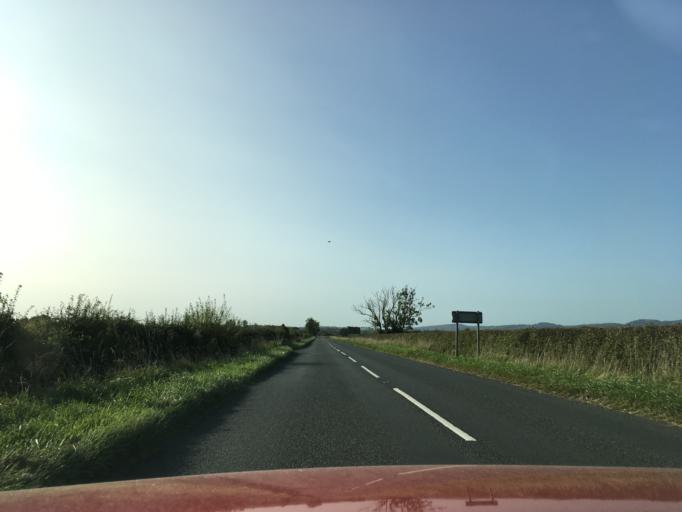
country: GB
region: England
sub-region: Gloucestershire
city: Gloucester
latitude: 51.9587
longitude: -2.2835
